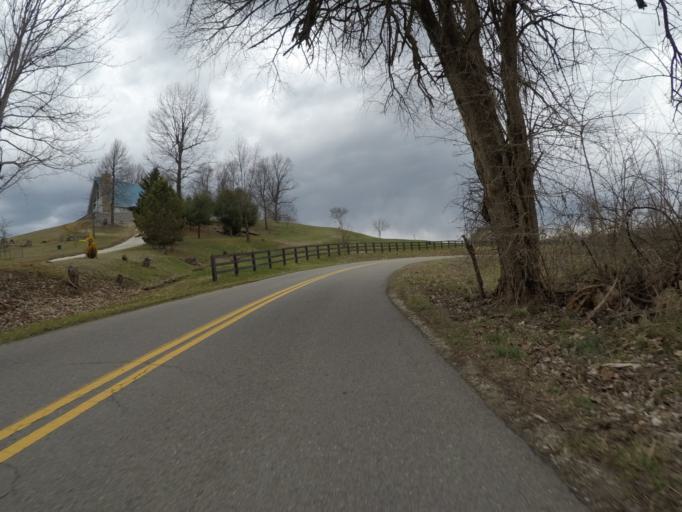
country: US
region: Ohio
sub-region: Lawrence County
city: Burlington
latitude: 38.4414
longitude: -82.5278
